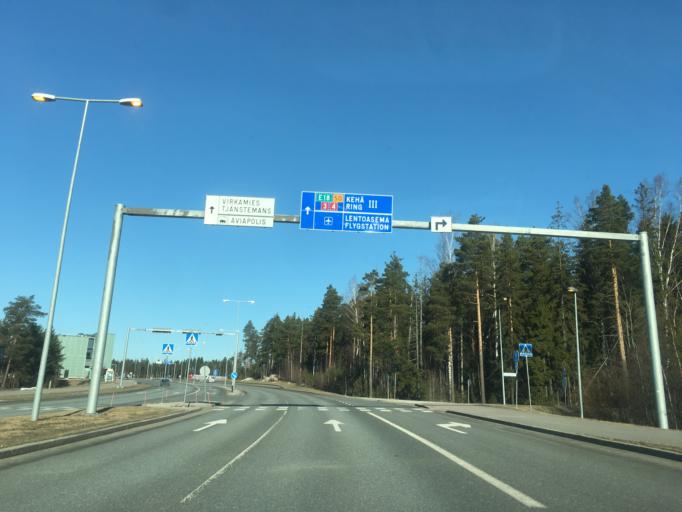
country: FI
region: Uusimaa
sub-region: Helsinki
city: Vantaa
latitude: 60.2995
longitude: 24.9684
